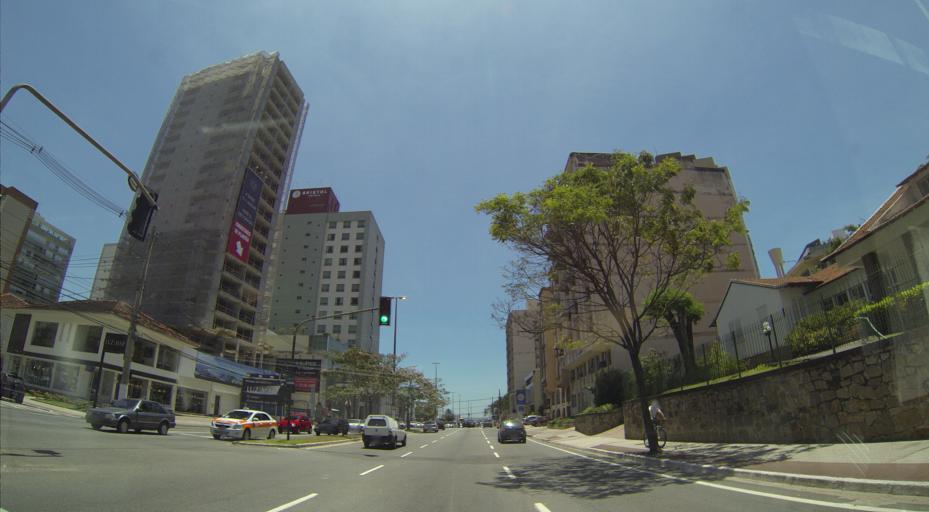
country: BR
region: Espirito Santo
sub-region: Vila Velha
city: Vila Velha
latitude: -20.2977
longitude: -40.2914
